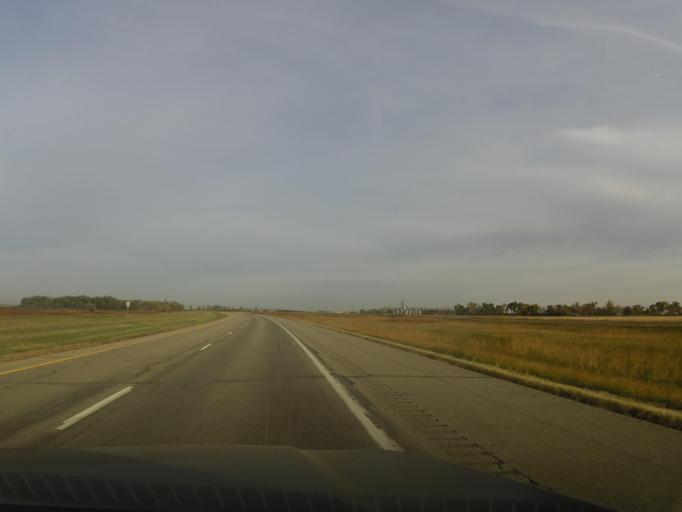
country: US
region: Minnesota
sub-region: Kittson County
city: Hallock
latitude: 48.7530
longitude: -97.2039
